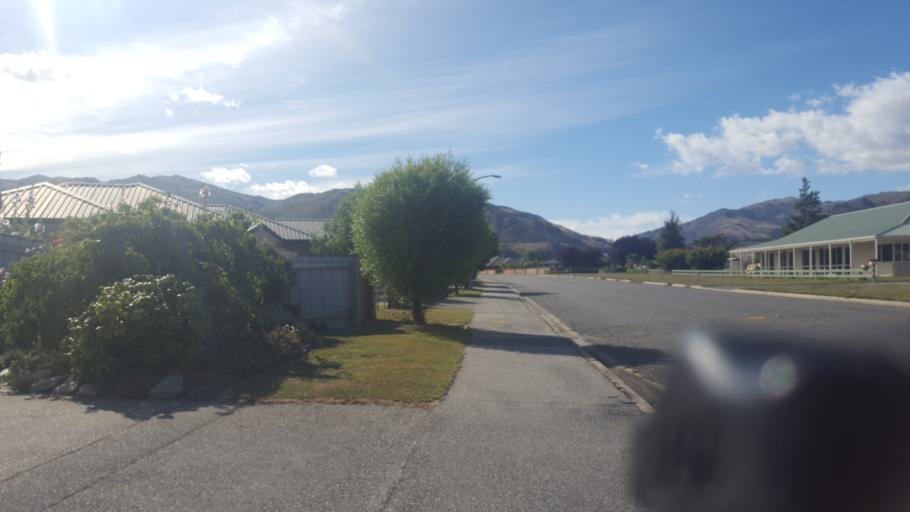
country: NZ
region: Otago
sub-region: Queenstown-Lakes District
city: Wanaka
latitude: -45.0473
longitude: 169.1984
